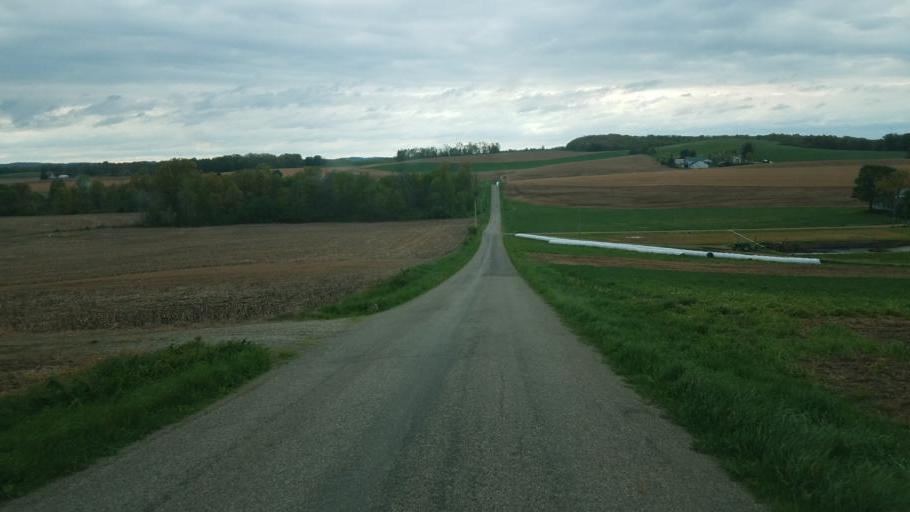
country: US
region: Ohio
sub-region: Ashland County
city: Loudonville
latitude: 40.6037
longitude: -82.3380
